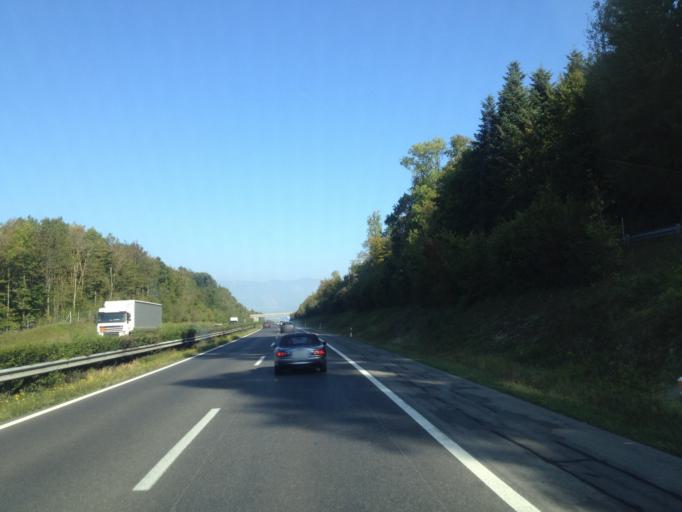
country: CH
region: Vaud
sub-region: Jura-Nord vaudois District
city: Bavois
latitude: 46.6616
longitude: 6.5725
